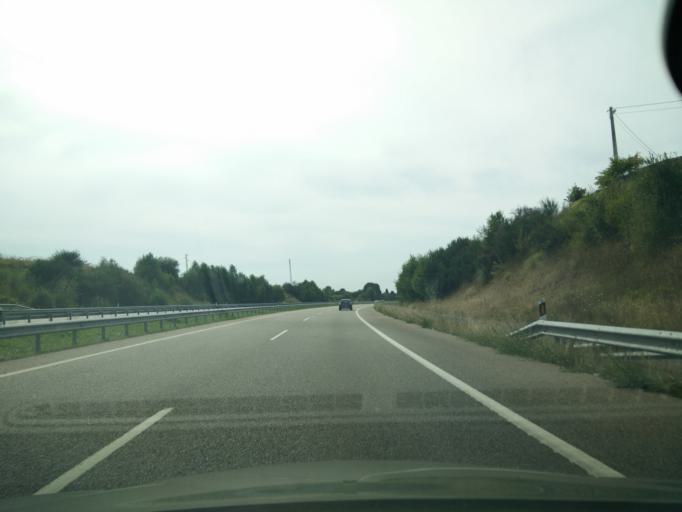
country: ES
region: Asturias
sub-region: Province of Asturias
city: Arriba
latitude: 43.5082
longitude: -5.5541
